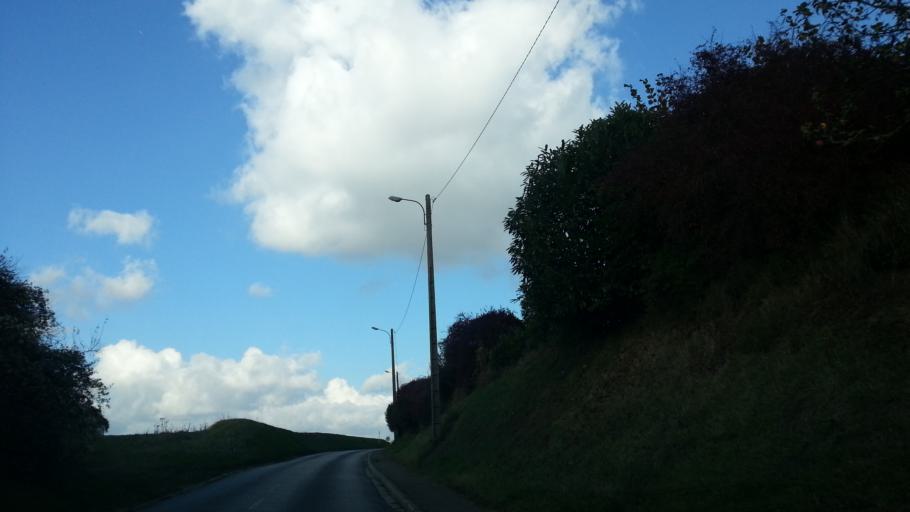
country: FR
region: Picardie
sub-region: Departement de l'Oise
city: Villers-sous-Saint-Leu
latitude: 49.2224
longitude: 2.4150
